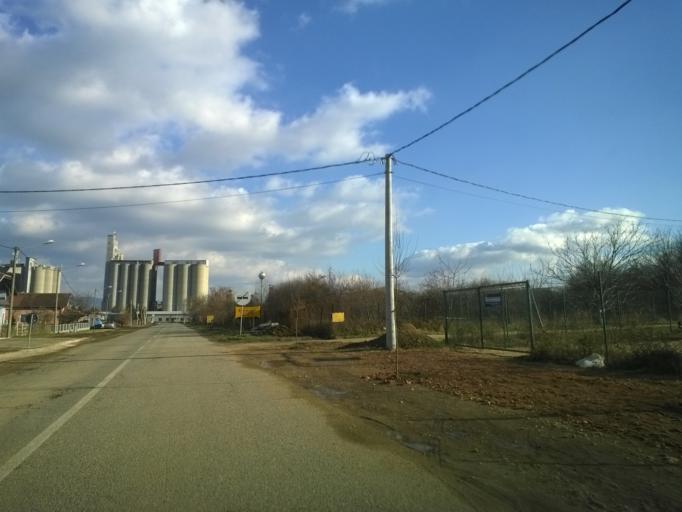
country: RS
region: Central Serbia
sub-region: Branicevski Okrug
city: Veliko Gradiste
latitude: 44.7552
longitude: 21.5128
